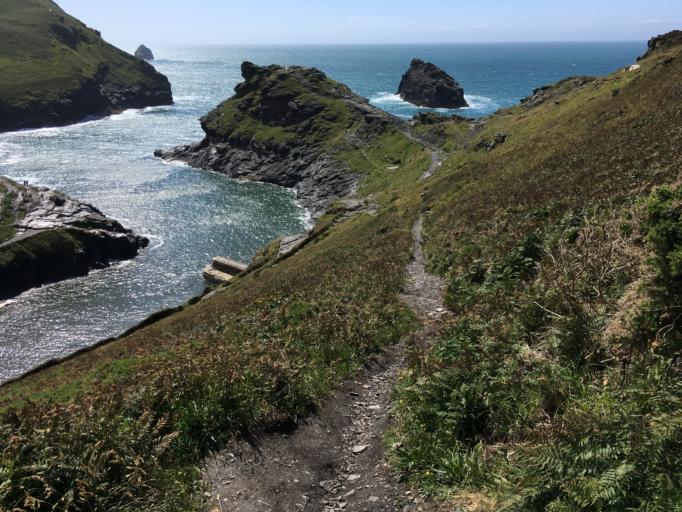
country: GB
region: England
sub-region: Cornwall
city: Tintagel
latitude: 50.6926
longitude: -4.6971
